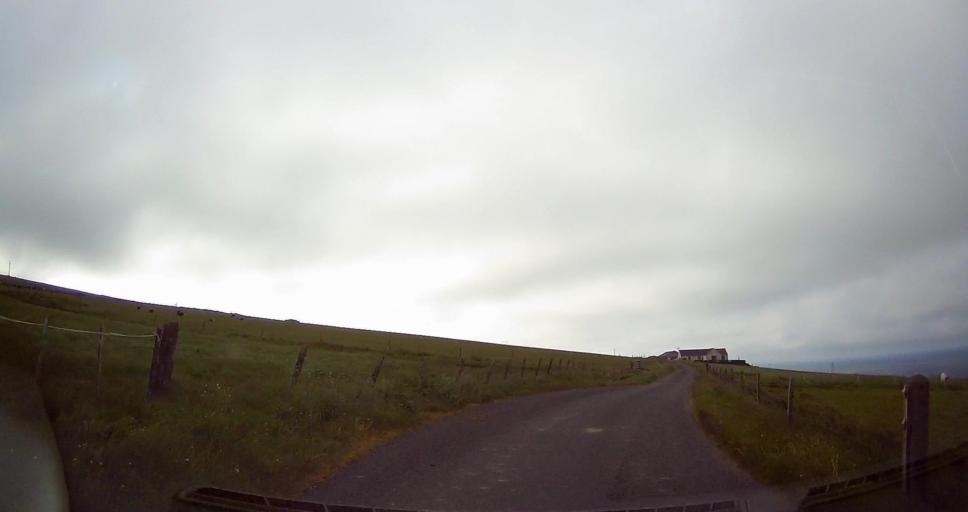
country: GB
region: Scotland
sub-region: Orkney Islands
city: Orkney
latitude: 59.1182
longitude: -3.1315
